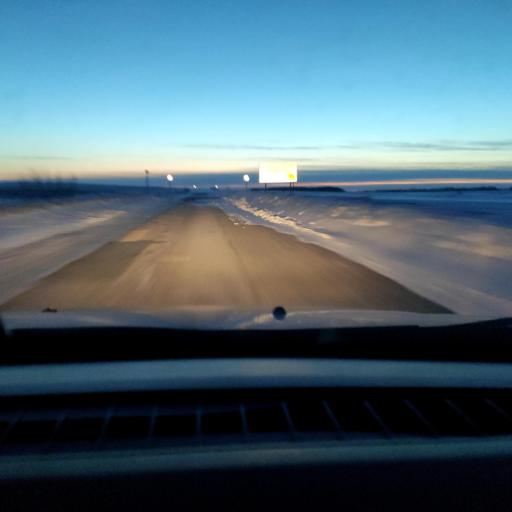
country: RU
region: Samara
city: Georgiyevka
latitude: 53.3073
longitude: 50.8161
